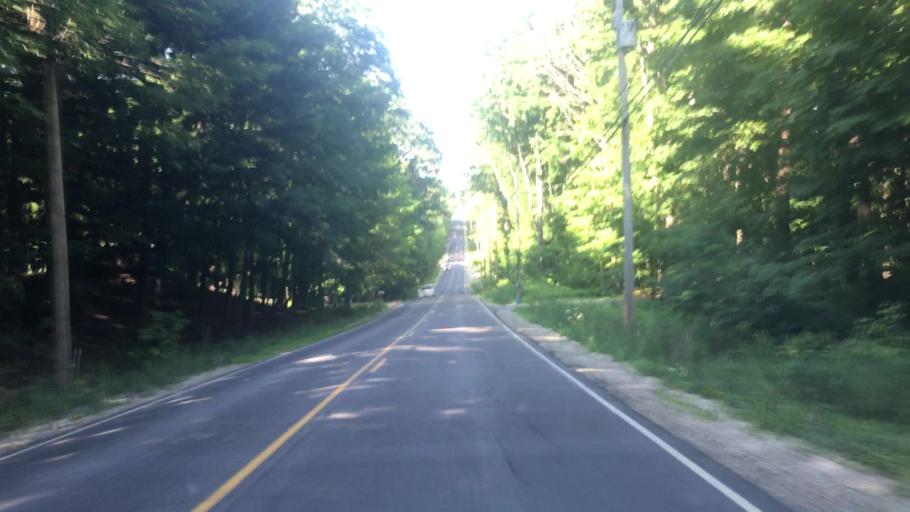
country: US
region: Maine
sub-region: York County
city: Buxton
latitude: 43.7264
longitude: -70.5602
